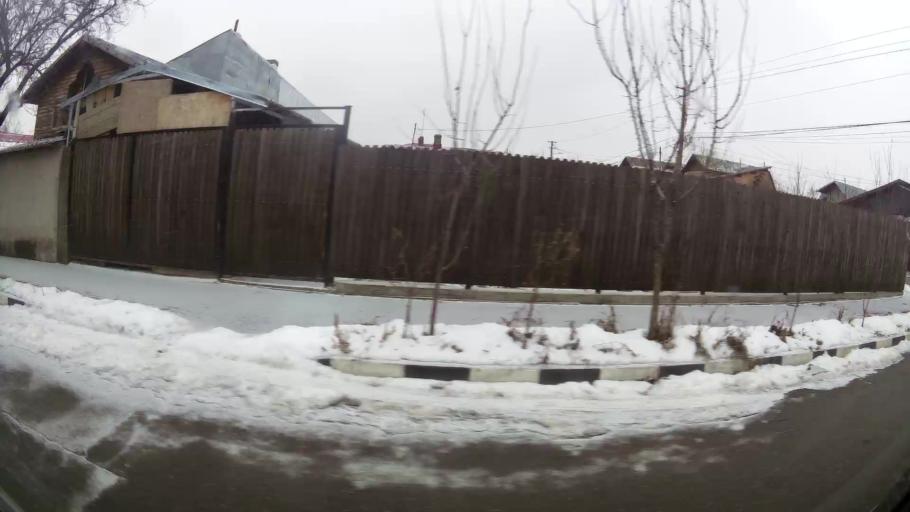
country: RO
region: Prahova
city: Ploiesti
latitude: 44.9549
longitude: 26.0372
